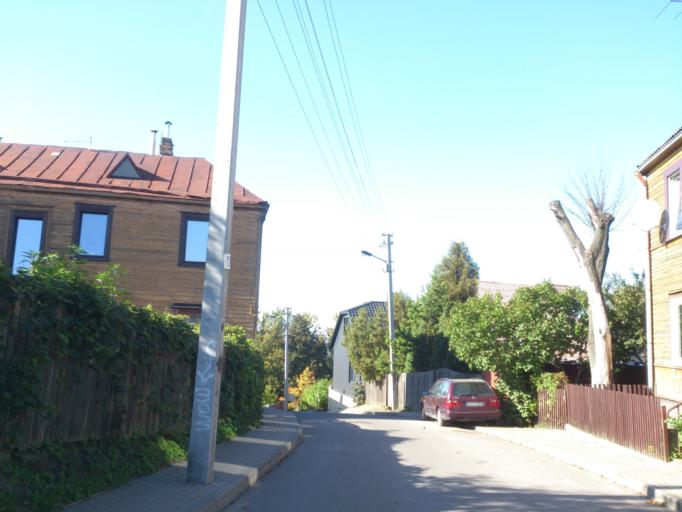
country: LT
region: Kauno apskritis
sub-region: Kaunas
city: Kaunas
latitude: 54.9044
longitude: 23.9047
